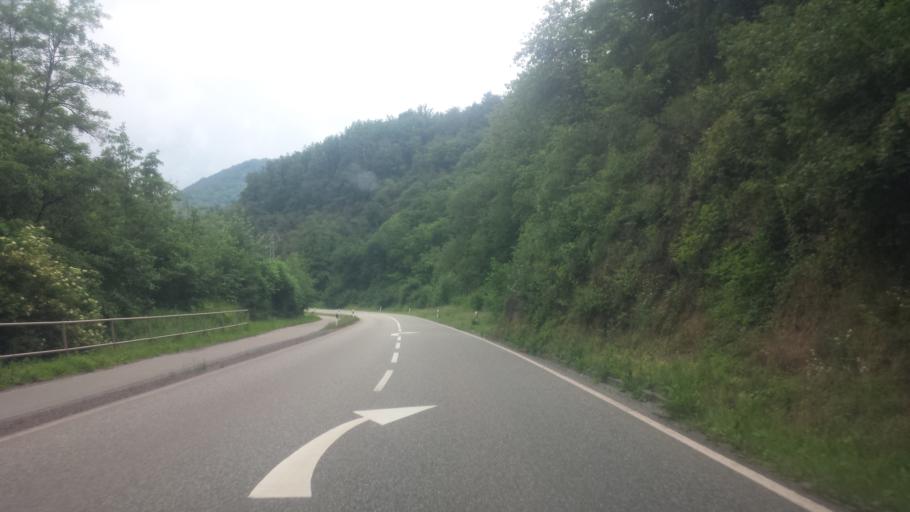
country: DE
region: Rheinland-Pfalz
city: Eschbach
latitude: 49.1612
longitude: 8.0058
